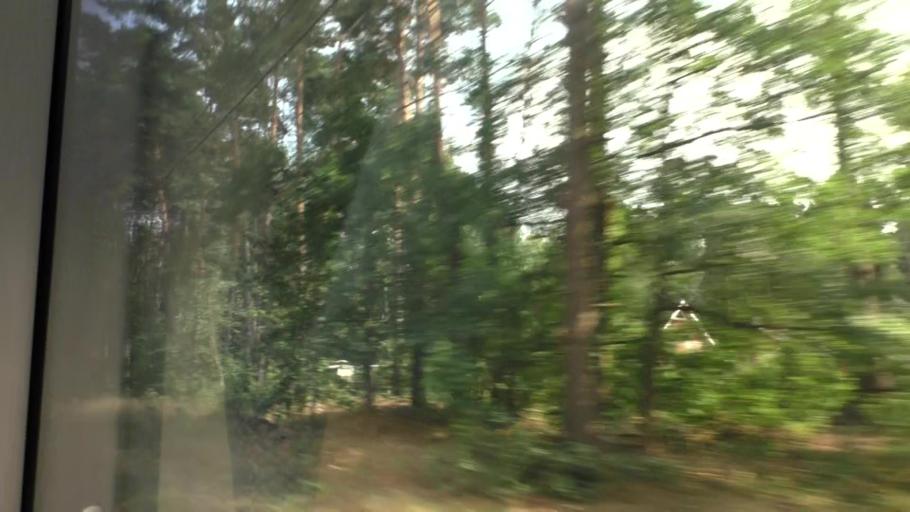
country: DE
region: Brandenburg
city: Wendisch Rietz
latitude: 52.2028
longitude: 14.0278
